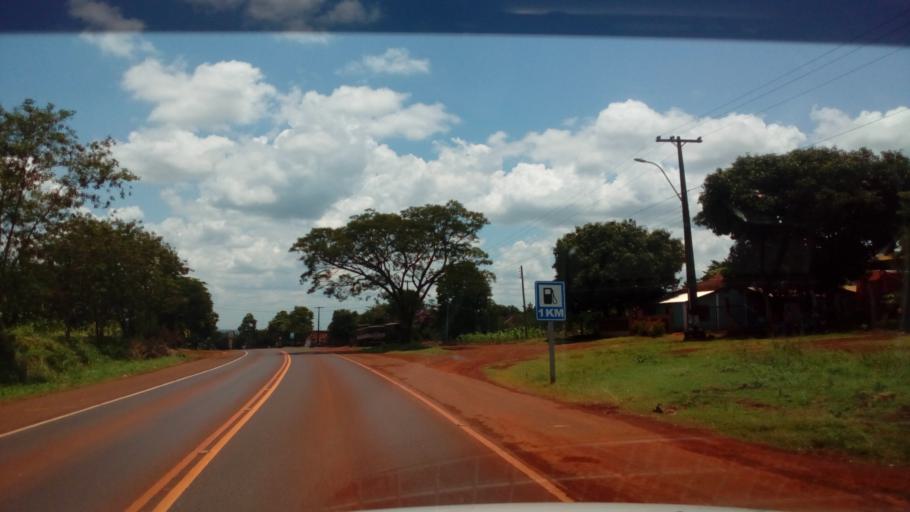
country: PY
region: Itapua
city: Edelira
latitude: -26.7626
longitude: -55.3840
